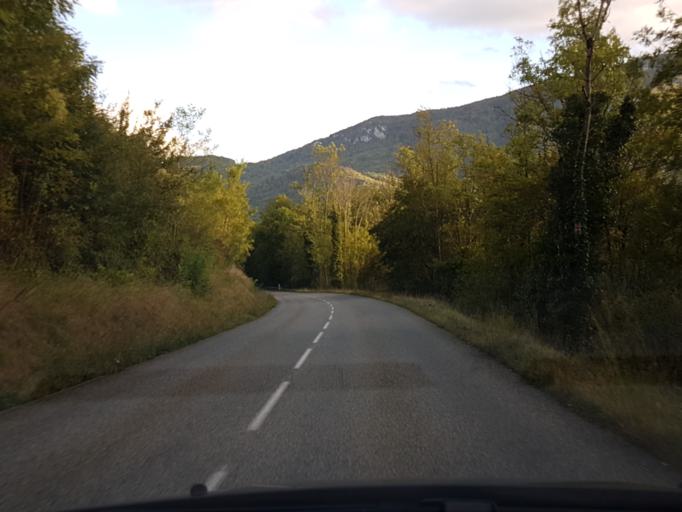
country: FR
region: Midi-Pyrenees
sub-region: Departement de l'Ariege
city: Tarascon-sur-Ariege
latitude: 42.8652
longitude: 1.5698
